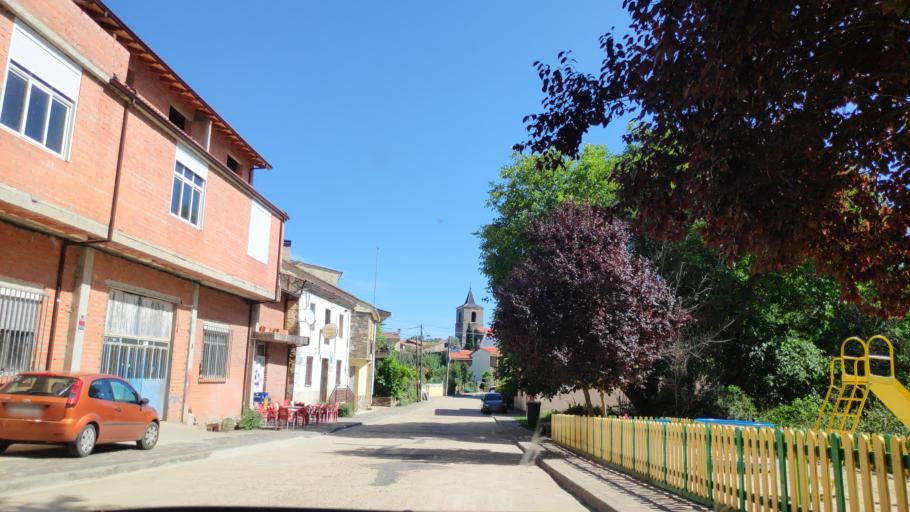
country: ES
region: Castille and Leon
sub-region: Provincia de Zamora
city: Rabano de Aliste
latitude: 41.7299
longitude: -6.4557
